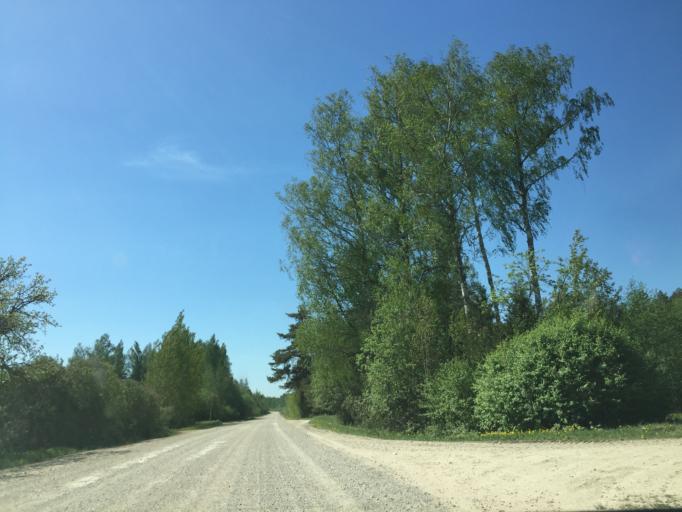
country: LV
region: Kegums
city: Kegums
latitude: 56.8834
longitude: 24.7867
